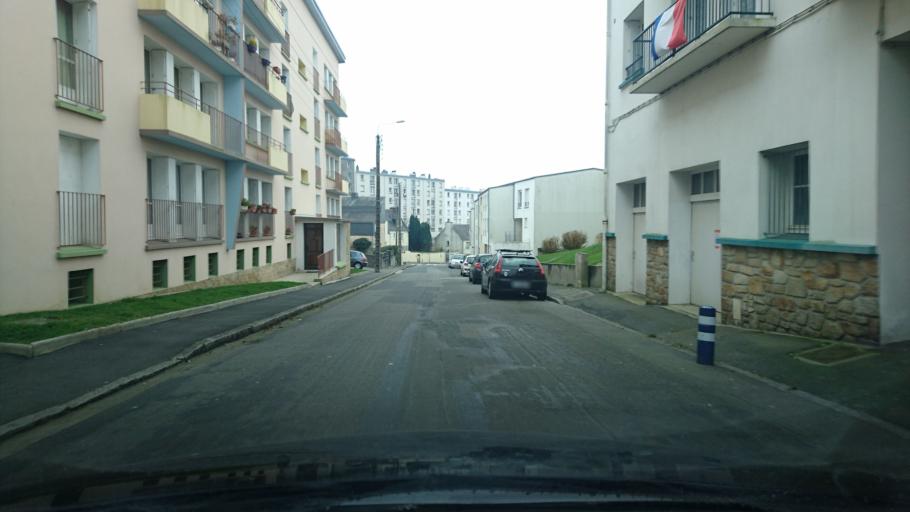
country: FR
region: Brittany
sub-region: Departement du Finistere
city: Brest
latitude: 48.3854
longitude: -4.5083
